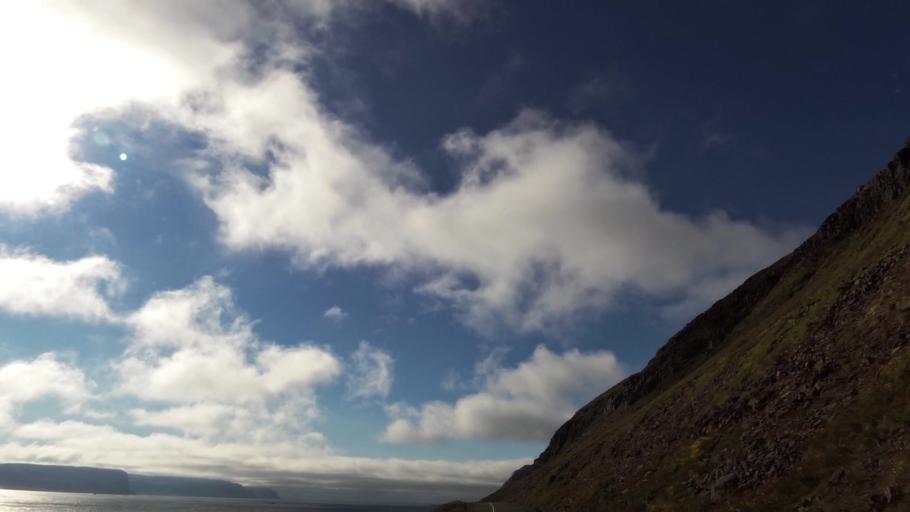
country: IS
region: West
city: Olafsvik
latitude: 65.5669
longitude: -23.9243
